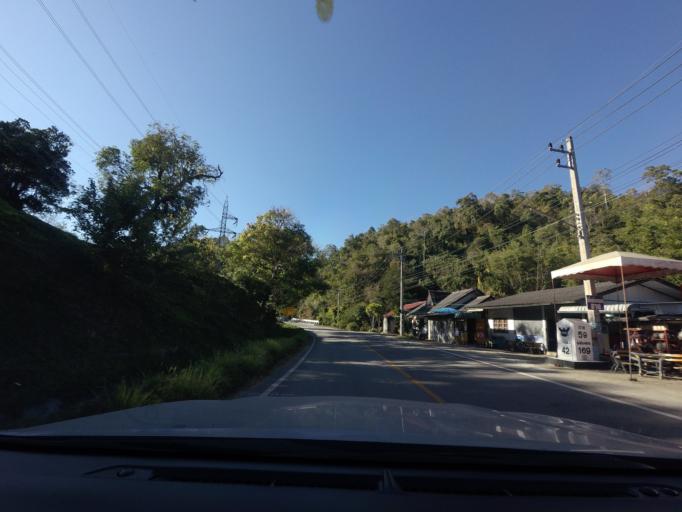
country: TH
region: Mae Hong Son
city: Mae Hi
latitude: 19.2053
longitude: 98.6767
